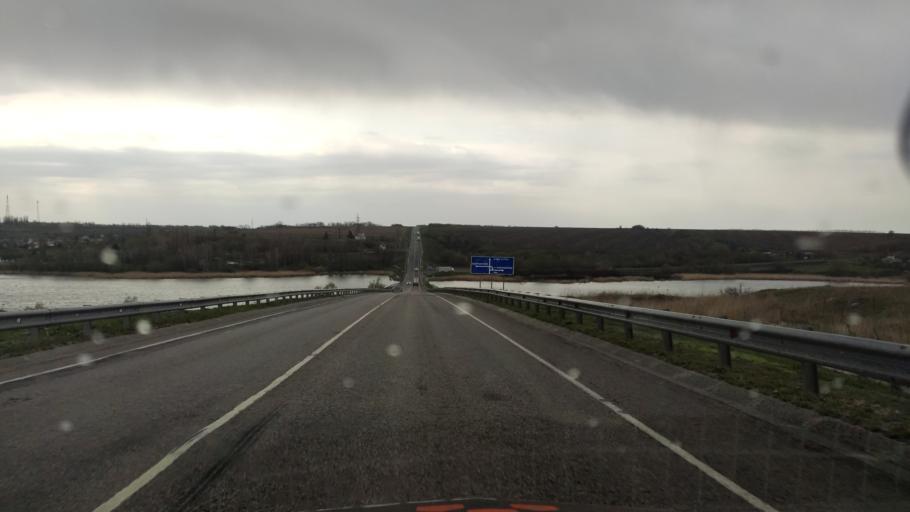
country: RU
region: Voronezj
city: Nizhnedevitsk
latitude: 51.5645
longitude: 38.3738
